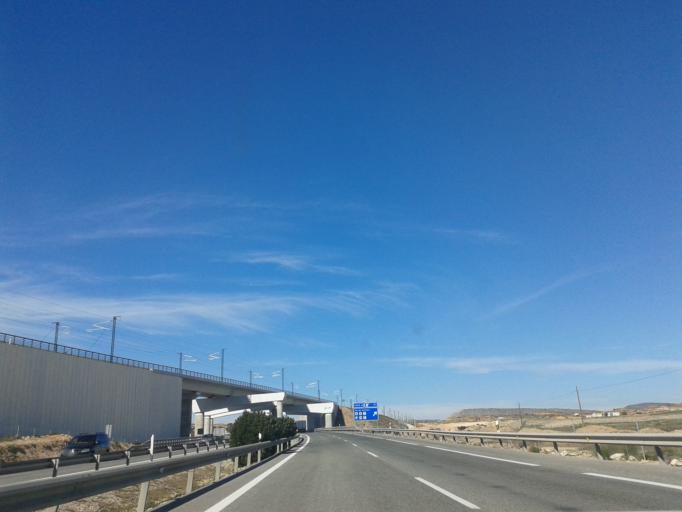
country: ES
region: Castille-La Mancha
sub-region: Provincia de Albacete
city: Caudete
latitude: 38.7193
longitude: -0.9316
